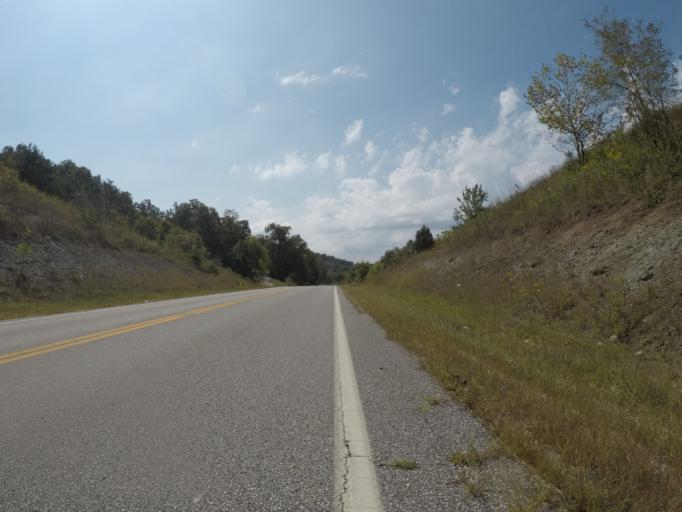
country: US
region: West Virginia
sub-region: Cabell County
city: Lesage
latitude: 38.5044
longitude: -82.3931
